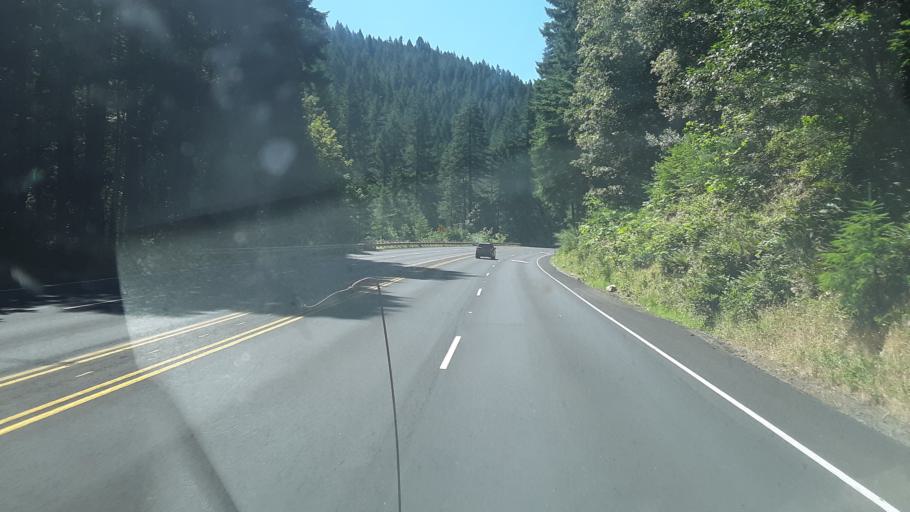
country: US
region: Oregon
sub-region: Josephine County
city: Cave Junction
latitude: 41.9098
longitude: -123.7691
